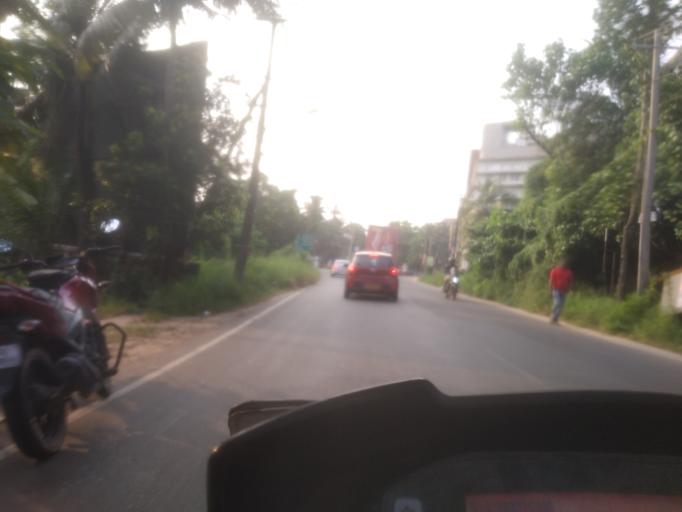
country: IN
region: Kerala
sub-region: Ernakulam
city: Cochin
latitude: 9.9423
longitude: 76.3360
